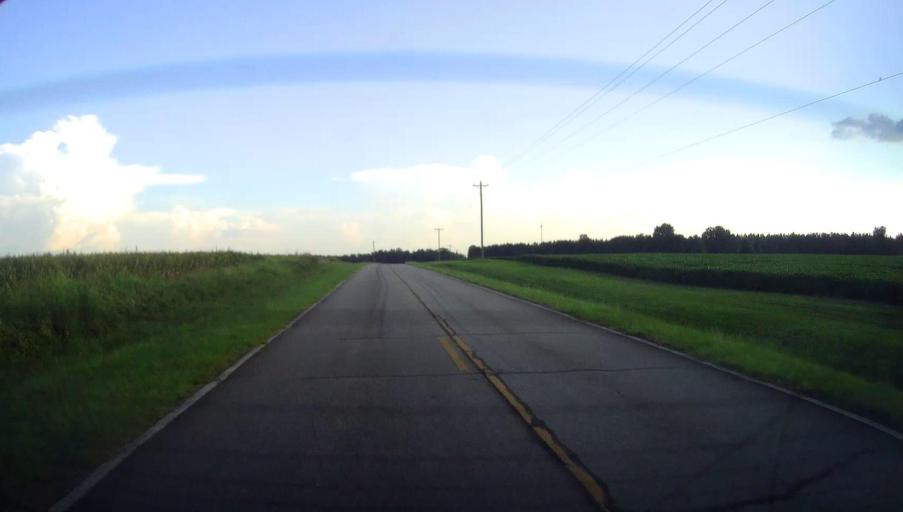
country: US
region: Georgia
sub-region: Peach County
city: Fort Valley
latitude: 32.6044
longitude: -83.8348
